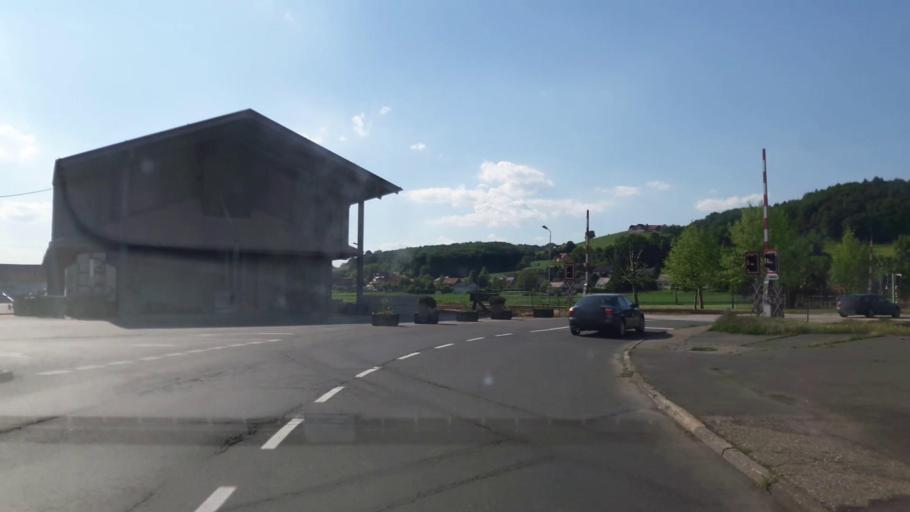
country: AT
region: Styria
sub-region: Politischer Bezirk Suedoststeiermark
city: Fehring
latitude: 46.9496
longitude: 16.0094
